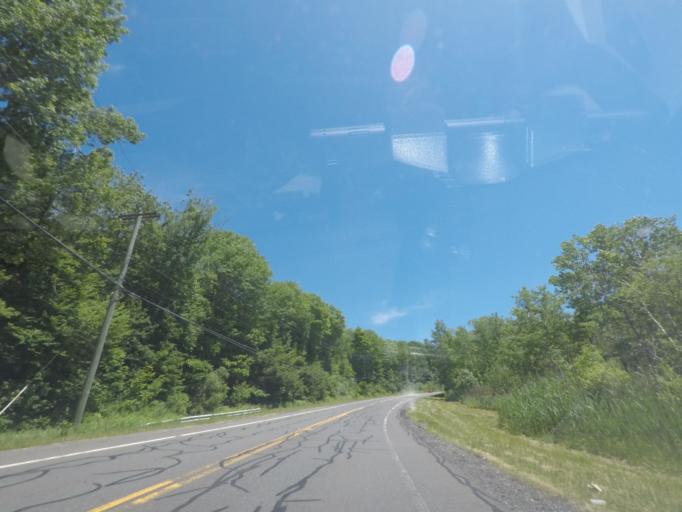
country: US
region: Massachusetts
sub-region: Berkshire County
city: Otis
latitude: 42.2606
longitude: -73.0944
